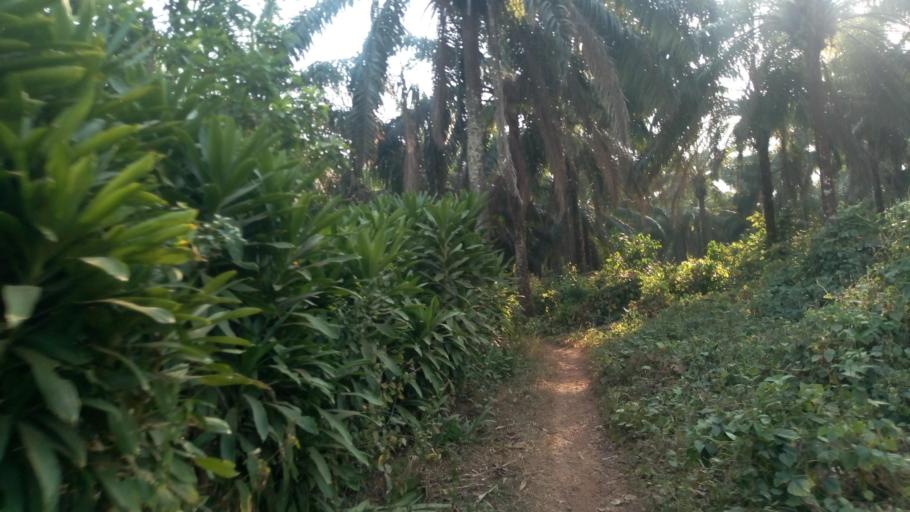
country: SL
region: Southern Province
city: Mogbwemo
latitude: 7.5995
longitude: -12.1721
